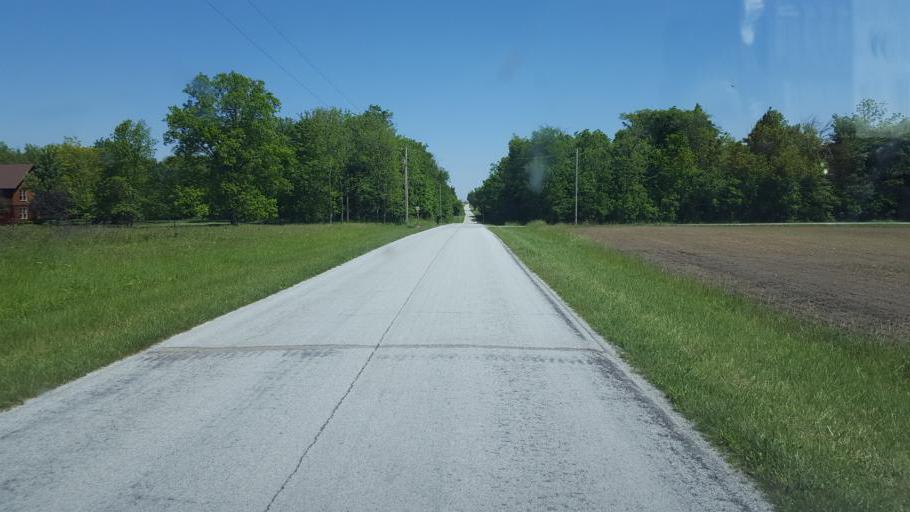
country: US
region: Ohio
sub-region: Hardin County
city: Forest
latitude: 40.6505
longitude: -83.4391
